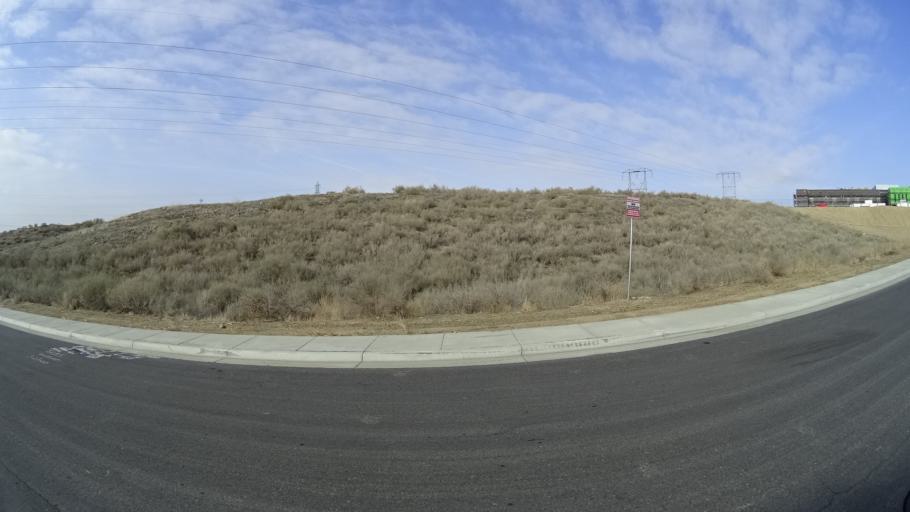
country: US
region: California
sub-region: Kern County
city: Bakersfield
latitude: 35.3933
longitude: -118.9194
